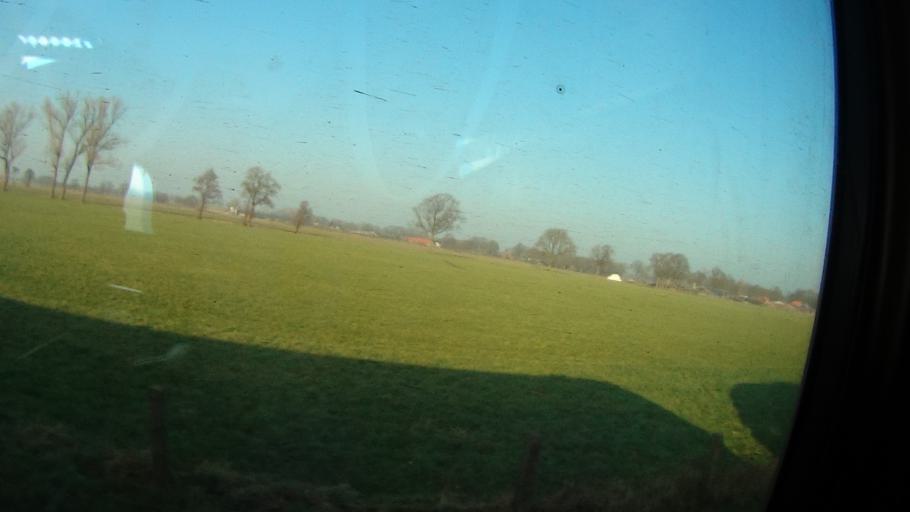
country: NL
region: Overijssel
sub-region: Gemeente Dalfsen
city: Dalfsen
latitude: 52.5057
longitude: 6.1936
